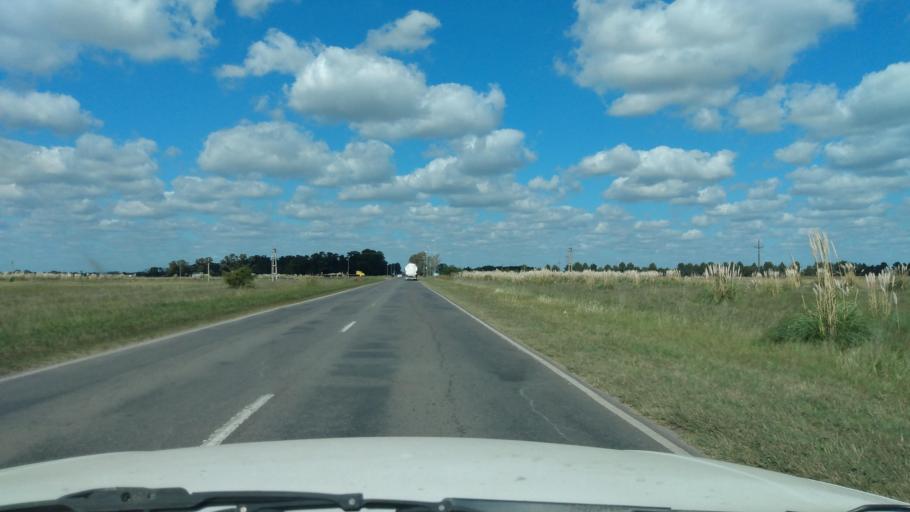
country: AR
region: Buenos Aires
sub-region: Partido de Navarro
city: Navarro
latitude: -34.9834
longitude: -59.3158
